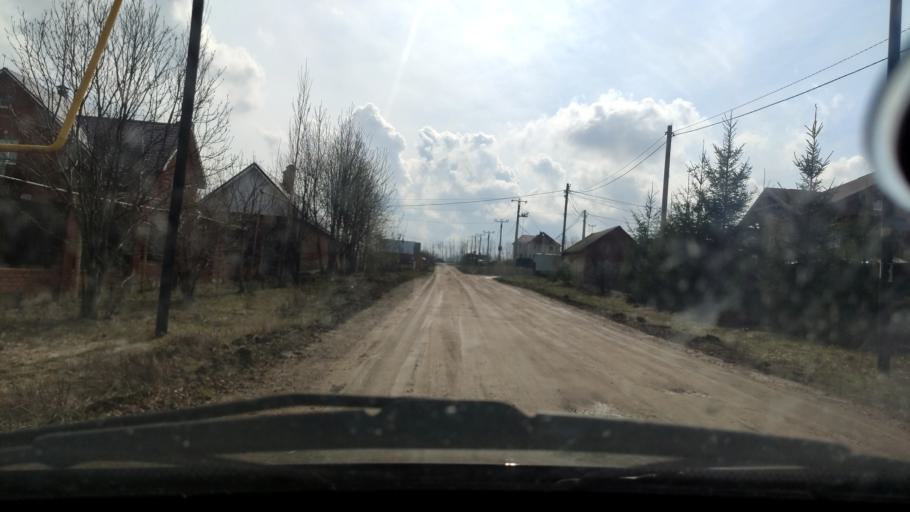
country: RU
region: Bashkortostan
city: Iglino
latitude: 54.7969
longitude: 56.2750
